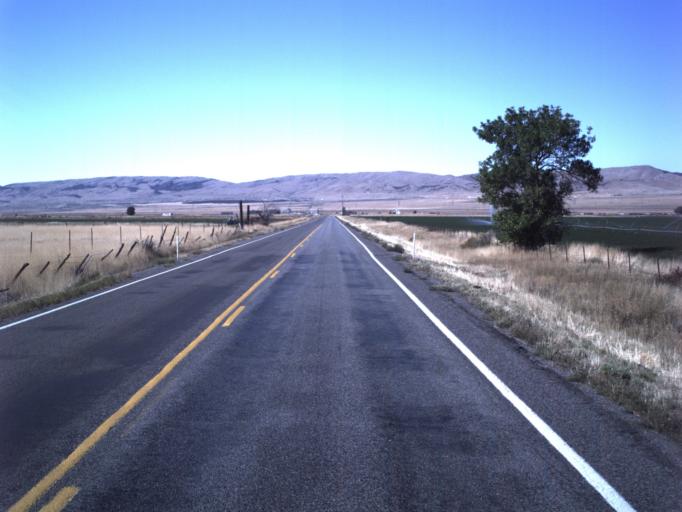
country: US
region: Utah
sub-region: Juab County
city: Nephi
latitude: 39.5583
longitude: -111.8734
